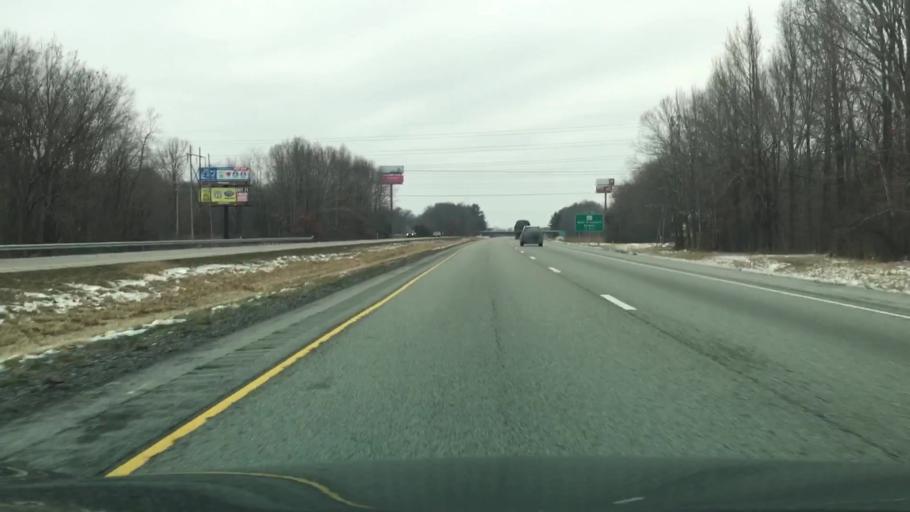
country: US
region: Illinois
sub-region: Franklin County
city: West Frankfort
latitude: 37.8865
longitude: -88.9439
